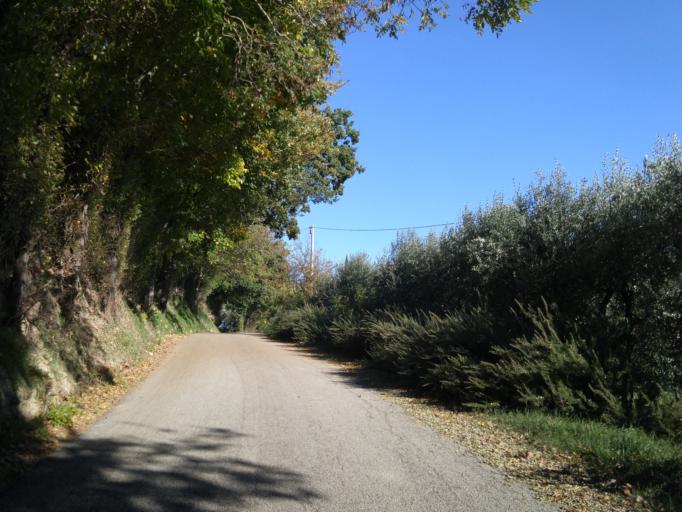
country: IT
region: The Marches
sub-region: Provincia di Pesaro e Urbino
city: Cartoceto
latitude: 43.7784
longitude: 12.8805
